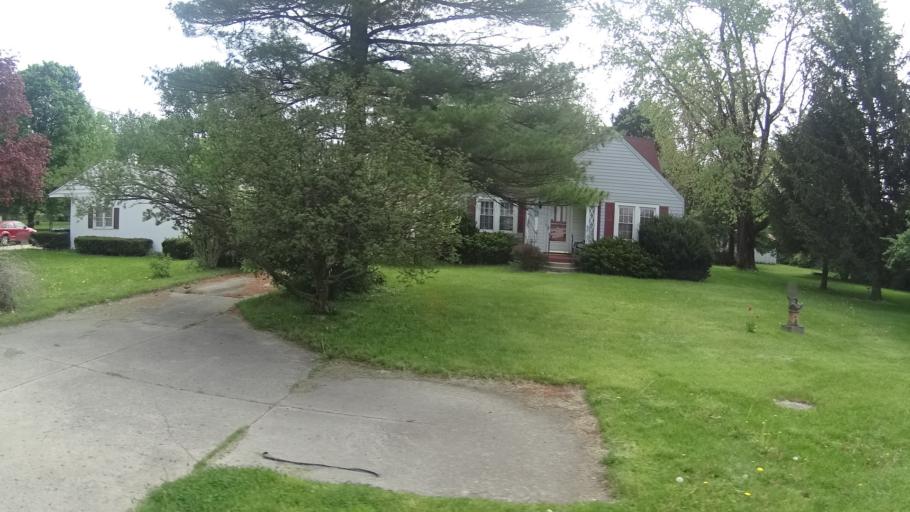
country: US
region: Indiana
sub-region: Madison County
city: Anderson
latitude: 40.1329
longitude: -85.6915
